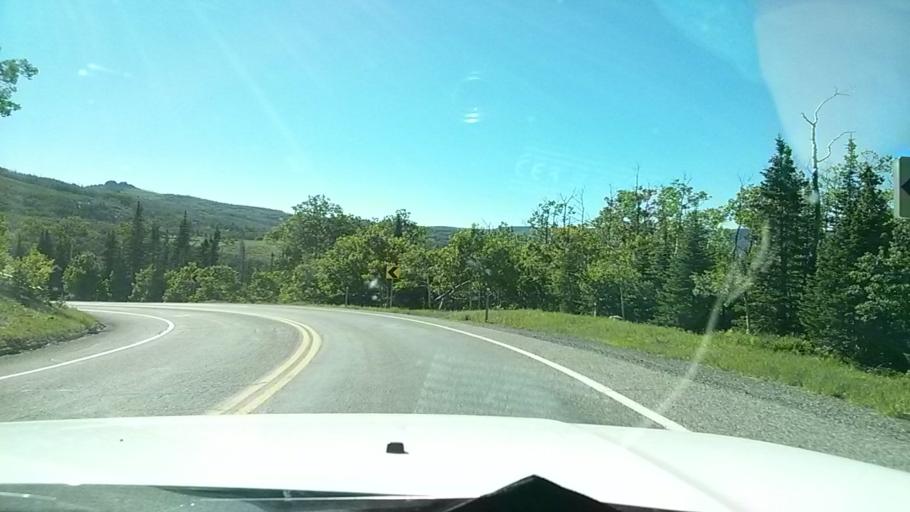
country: US
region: Utah
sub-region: Wayne County
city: Loa
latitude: 38.0687
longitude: -111.3303
